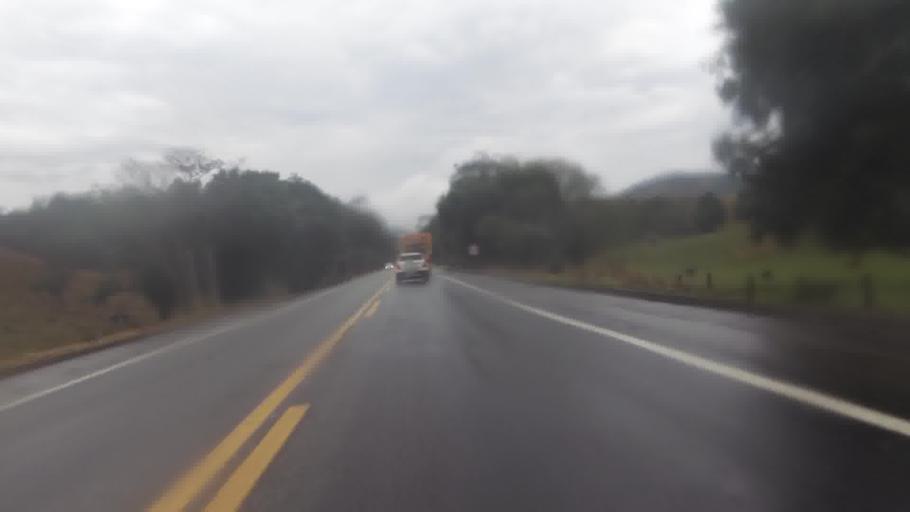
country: BR
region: Espirito Santo
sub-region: Cachoeiro De Itapemirim
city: Cachoeiro de Itapemirim
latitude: -21.0280
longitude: -41.1783
